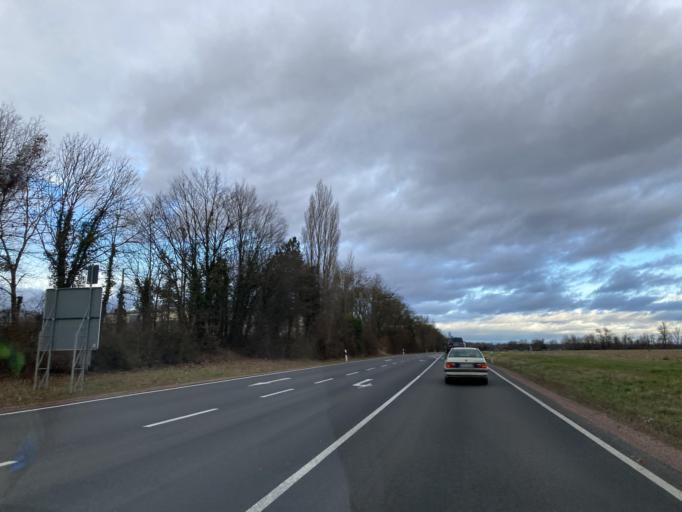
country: DE
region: Baden-Wuerttemberg
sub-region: Freiburg Region
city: Breisach am Rhein
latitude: 48.0347
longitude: 7.5931
